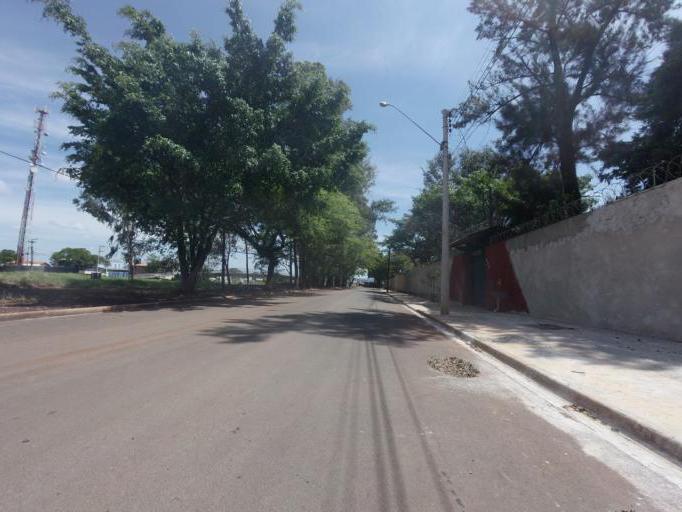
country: BR
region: Sao Paulo
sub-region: Piracicaba
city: Piracicaba
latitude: -22.7575
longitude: -47.5965
